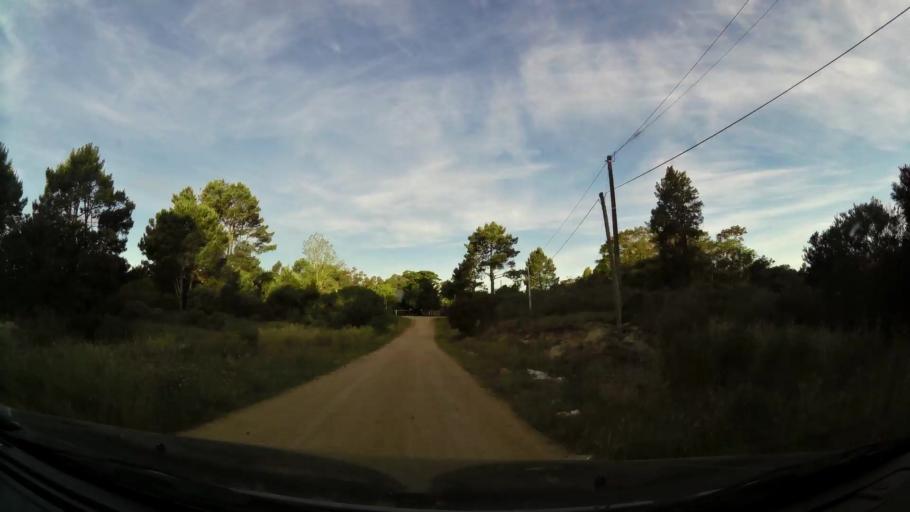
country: UY
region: Canelones
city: Atlantida
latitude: -34.7689
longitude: -55.8019
